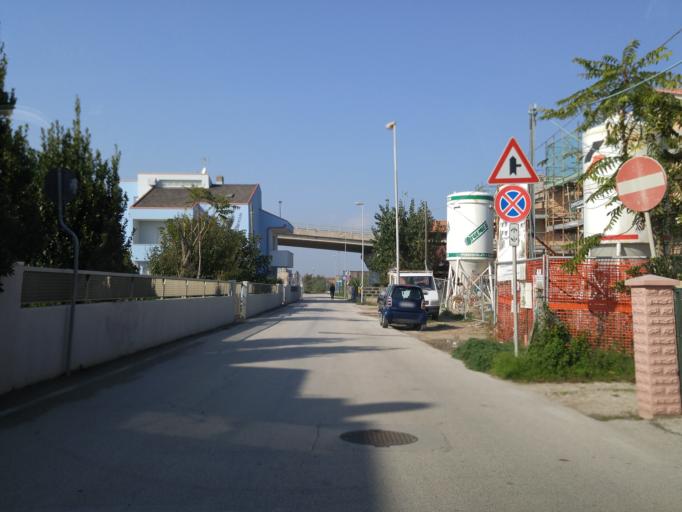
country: IT
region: The Marches
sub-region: Provincia di Pesaro e Urbino
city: Fano
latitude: 43.8374
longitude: 13.0376
